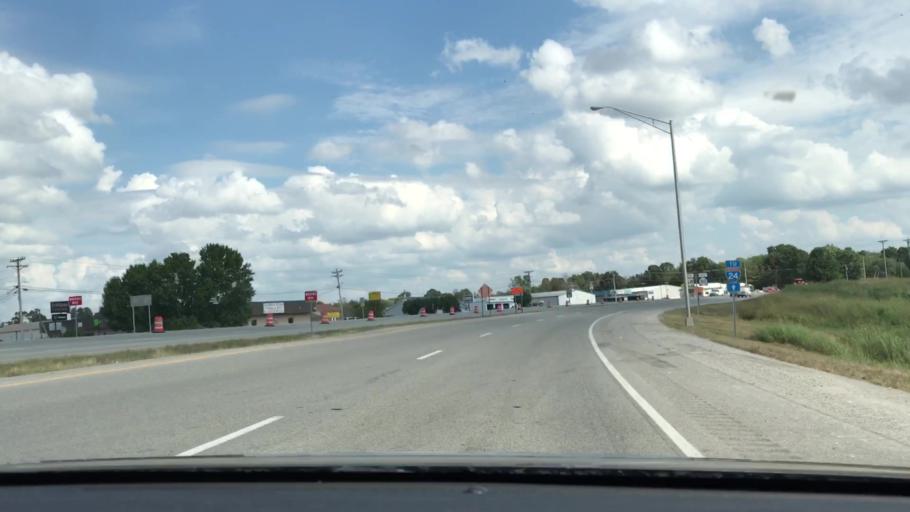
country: US
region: Kentucky
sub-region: Trigg County
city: Cadiz
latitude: 36.8663
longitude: -87.7958
